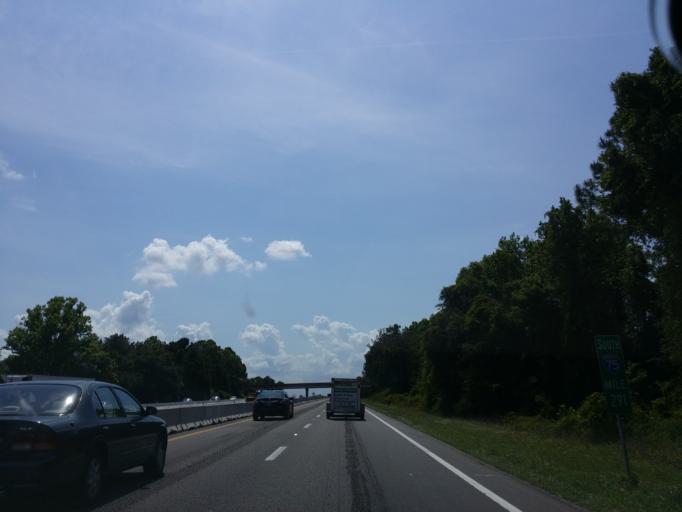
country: US
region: Florida
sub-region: Pasco County
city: San Antonio
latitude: 28.4031
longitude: -82.3092
